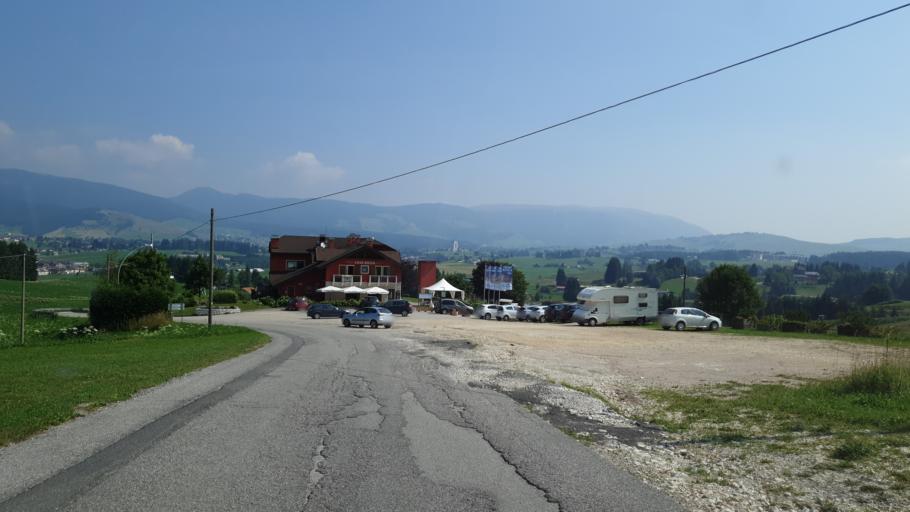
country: IT
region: Veneto
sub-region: Provincia di Vicenza
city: Canove di Roana
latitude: 45.8521
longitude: 11.4945
